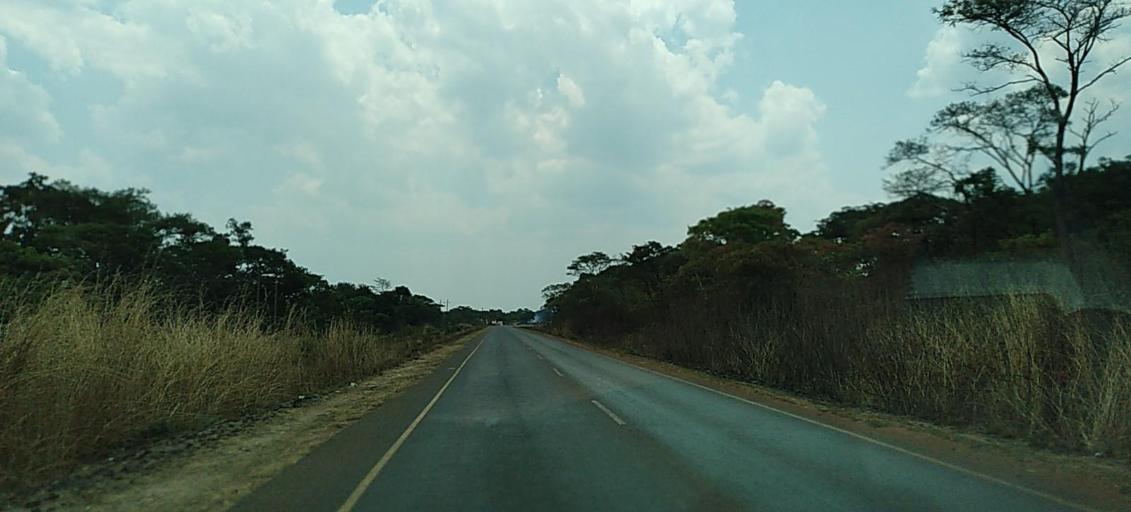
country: ZM
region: Copperbelt
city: Kalulushi
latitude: -12.8446
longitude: 28.0176
